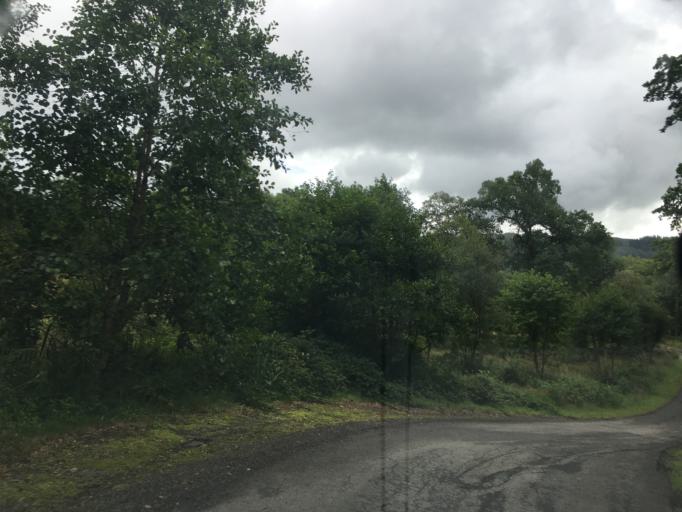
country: GB
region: Scotland
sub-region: Argyll and Bute
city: Oban
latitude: 56.2867
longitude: -5.3221
